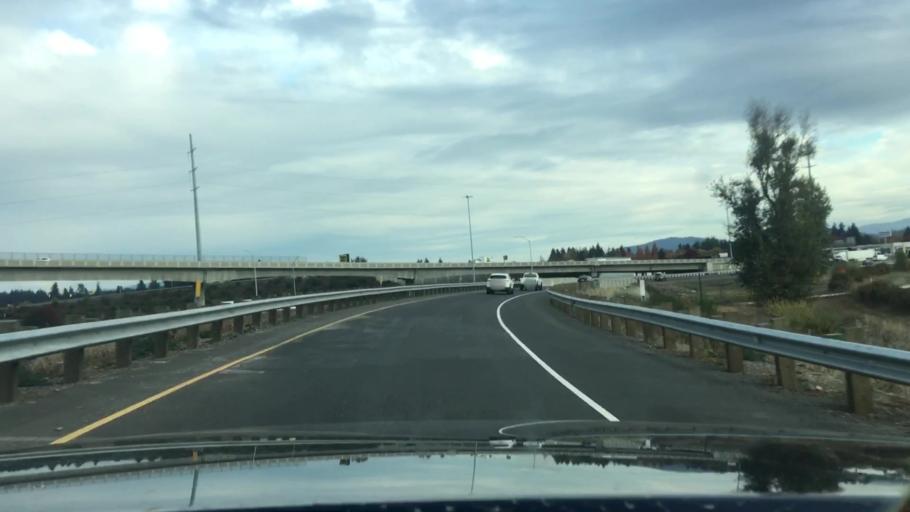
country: US
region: Oregon
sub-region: Lane County
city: Springfield
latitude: 44.0834
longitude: -123.0491
